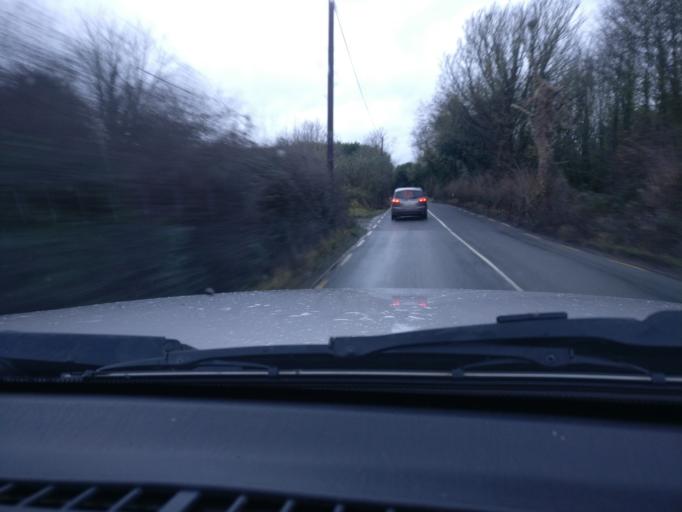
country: IE
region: Leinster
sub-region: An Mhi
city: Longwood
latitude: 53.4853
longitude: -6.8901
